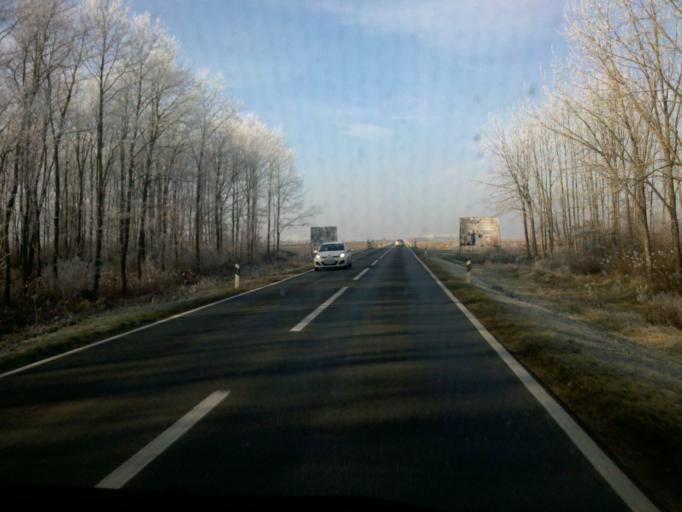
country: HR
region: Koprivnicko-Krizevacka
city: Kalinovac
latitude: 45.9986
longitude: 17.1189
